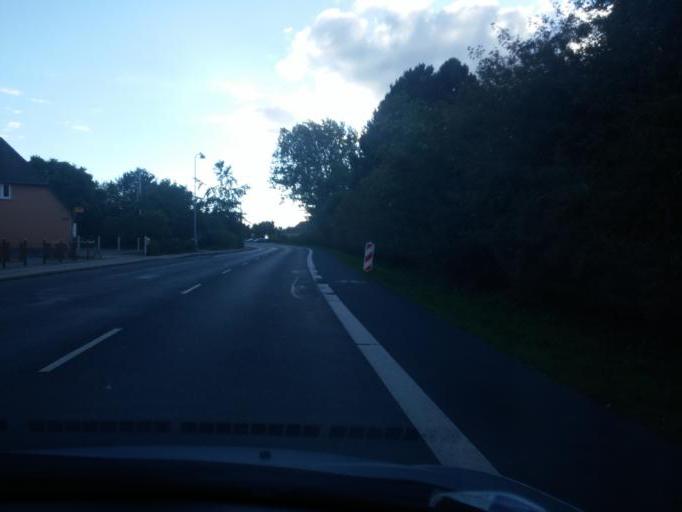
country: DK
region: South Denmark
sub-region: Odense Kommune
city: Bellinge
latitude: 55.3519
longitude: 10.3407
